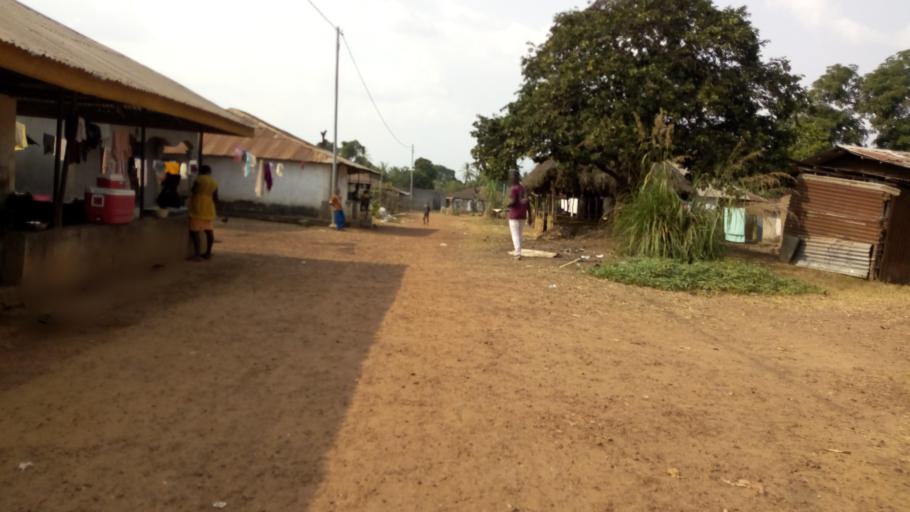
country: SL
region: Southern Province
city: Mogbwemo
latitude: 7.7637
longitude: -12.3084
